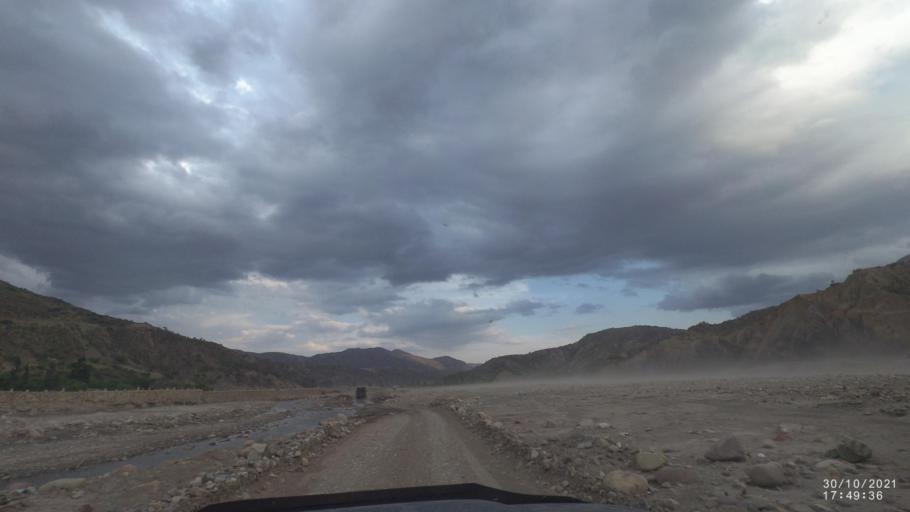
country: BO
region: Cochabamba
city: Sipe Sipe
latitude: -17.5361
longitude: -66.5136
